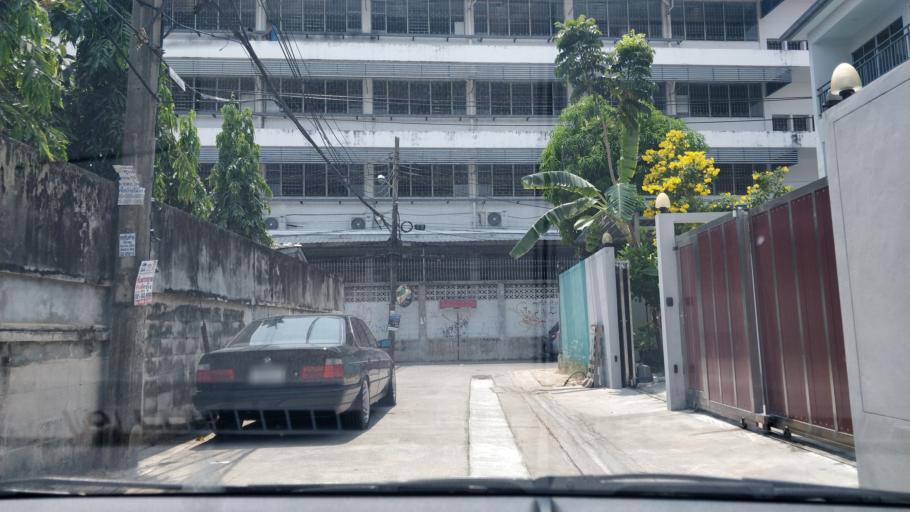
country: TH
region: Bangkok
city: Watthana
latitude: 13.7292
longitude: 100.6011
